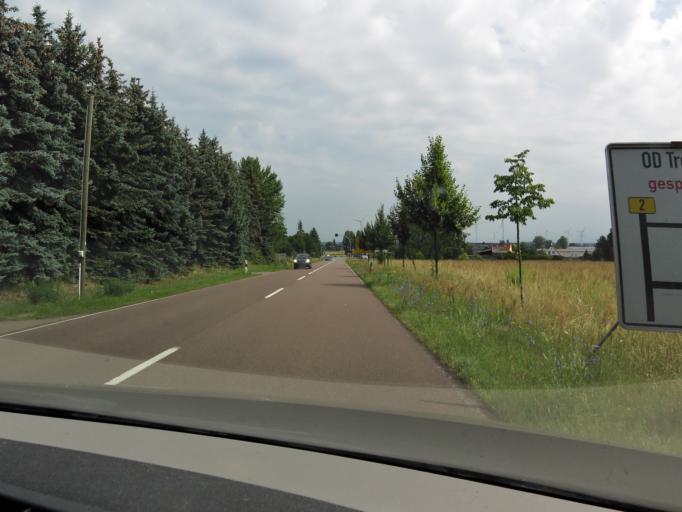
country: DE
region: Saxony-Anhalt
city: Kemberg
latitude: 51.7625
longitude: 12.6362
